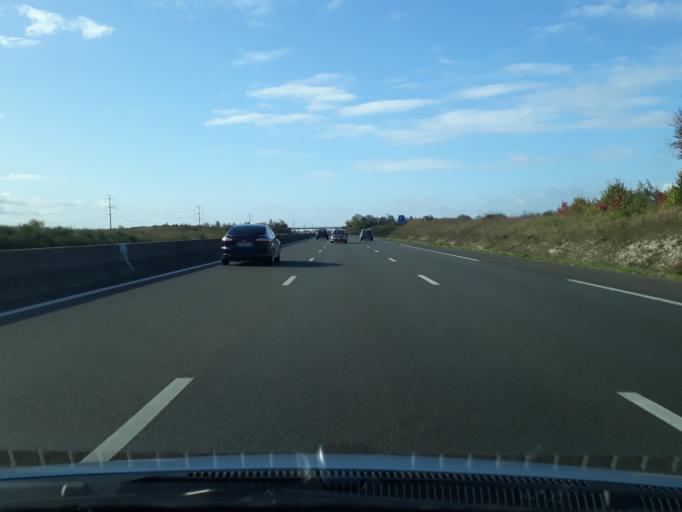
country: FR
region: Centre
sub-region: Departement du Loiret
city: Saint-Ay
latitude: 47.8809
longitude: 1.7404
